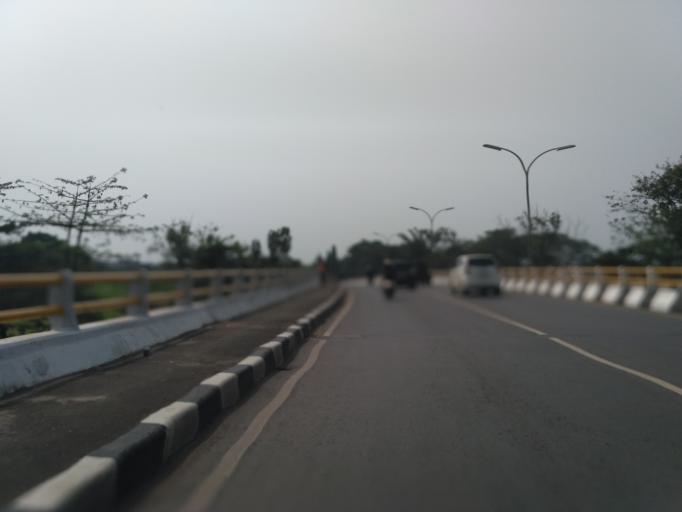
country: ID
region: Central Java
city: Semarang
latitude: -6.9792
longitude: 110.3876
